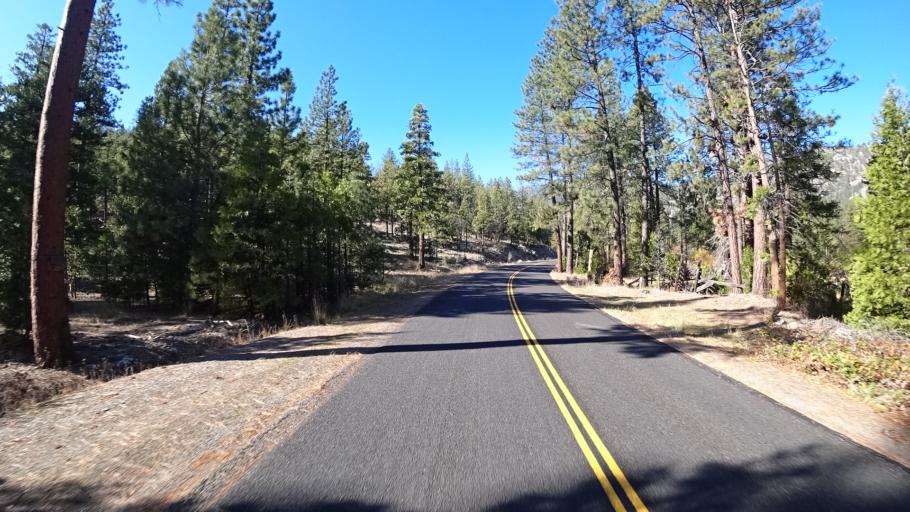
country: US
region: California
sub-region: Siskiyou County
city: Weed
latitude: 41.4324
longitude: -122.4902
